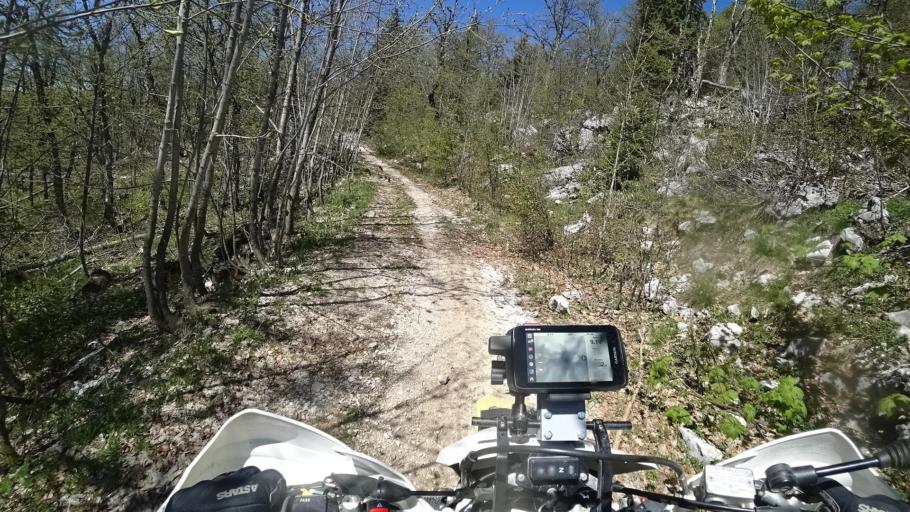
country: BA
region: Federation of Bosnia and Herzegovina
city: Rumboci
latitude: 43.8717
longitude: 17.4638
